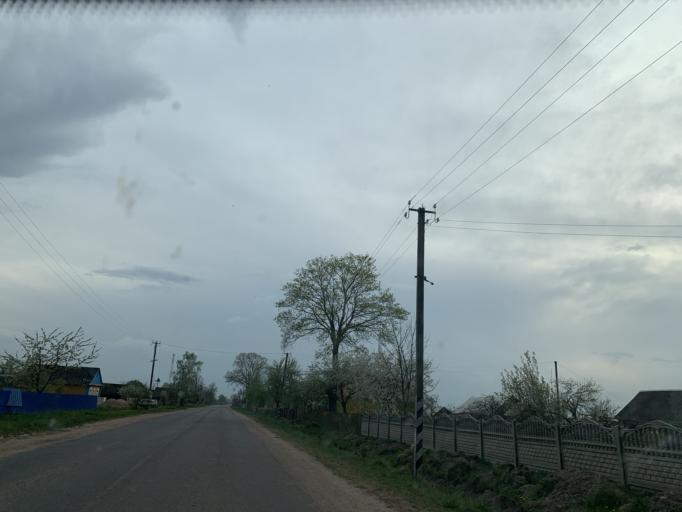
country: BY
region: Minsk
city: Kapyl'
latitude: 53.2835
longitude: 26.9815
